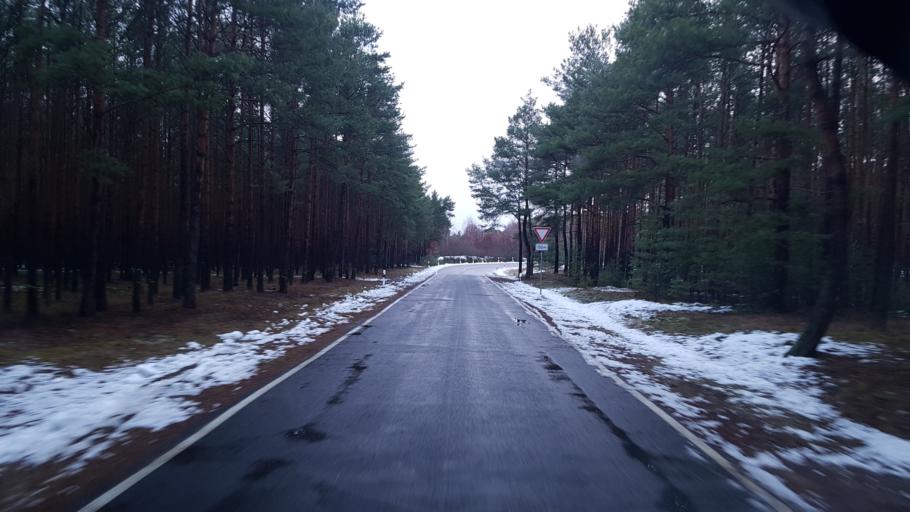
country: DE
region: Brandenburg
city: Janschwalde
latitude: 51.8470
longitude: 14.5073
